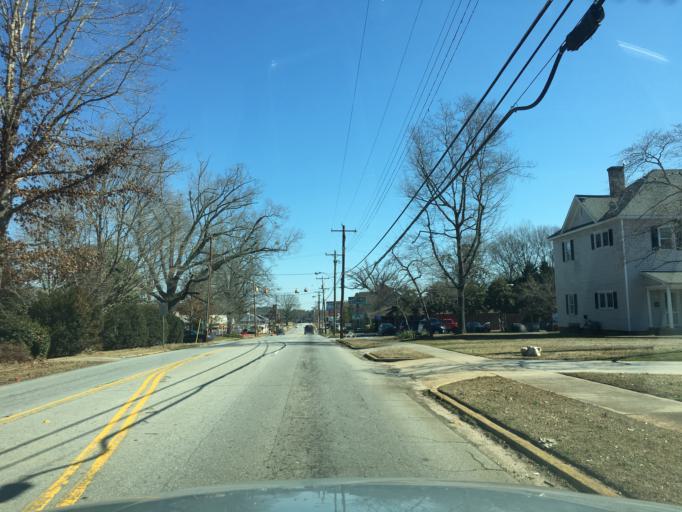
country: US
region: South Carolina
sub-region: Pickens County
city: Liberty
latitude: 34.7867
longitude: -82.7003
